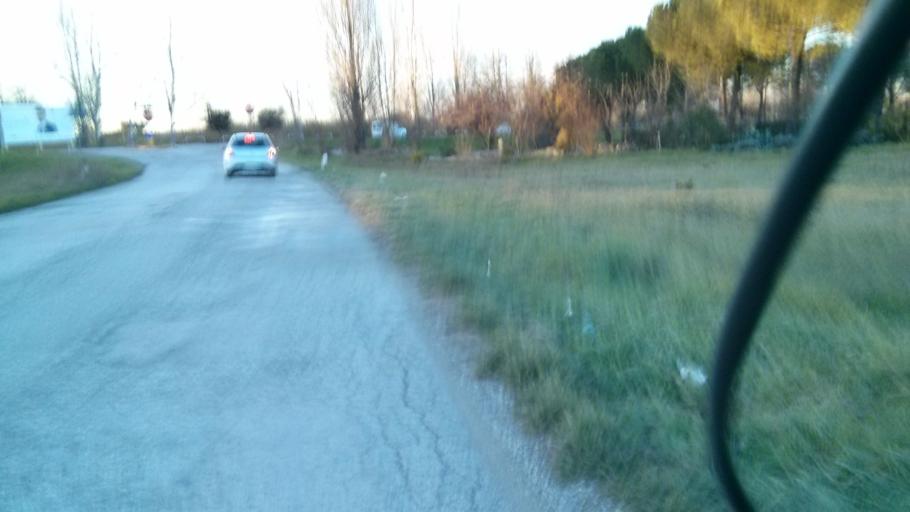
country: IT
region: The Marches
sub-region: Provincia di Pesaro e Urbino
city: Fano
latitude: 43.8286
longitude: 13.0159
